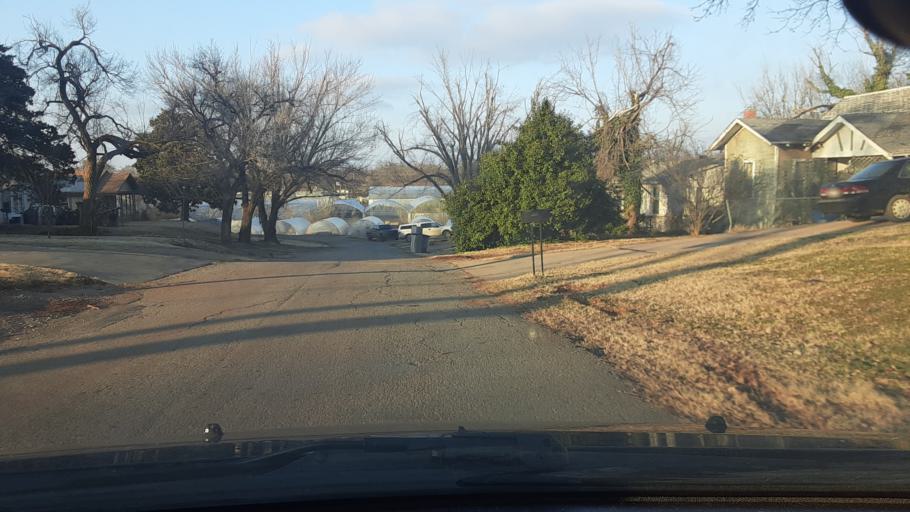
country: US
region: Oklahoma
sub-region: Logan County
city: Guthrie
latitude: 35.8866
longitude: -97.4215
